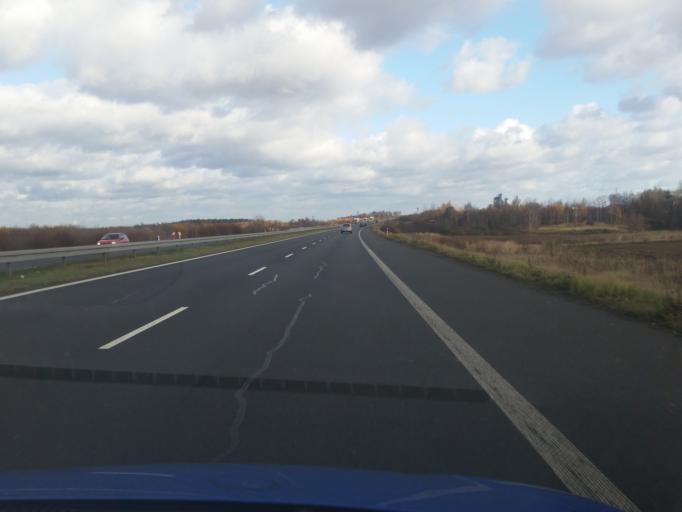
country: PL
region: Silesian Voivodeship
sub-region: Powiat czestochowski
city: Koscielec
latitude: 50.8823
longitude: 19.1675
